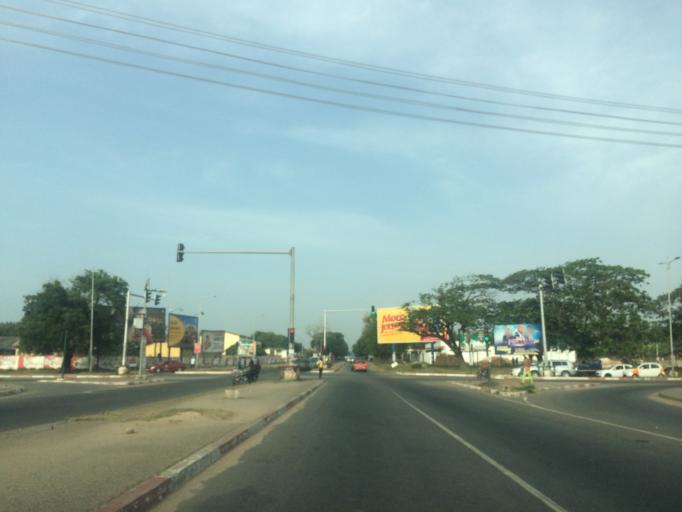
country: GH
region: Greater Accra
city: Accra
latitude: 5.5374
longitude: -0.2211
